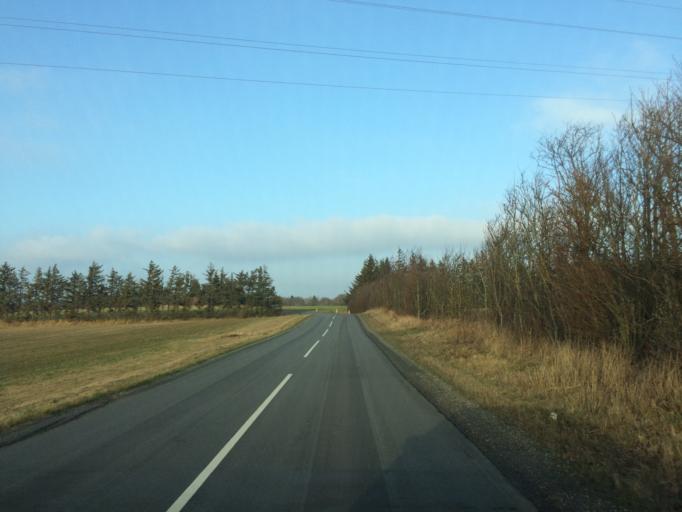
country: DK
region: South Denmark
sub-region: Varde Kommune
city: Oksbol
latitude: 55.7299
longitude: 8.2525
